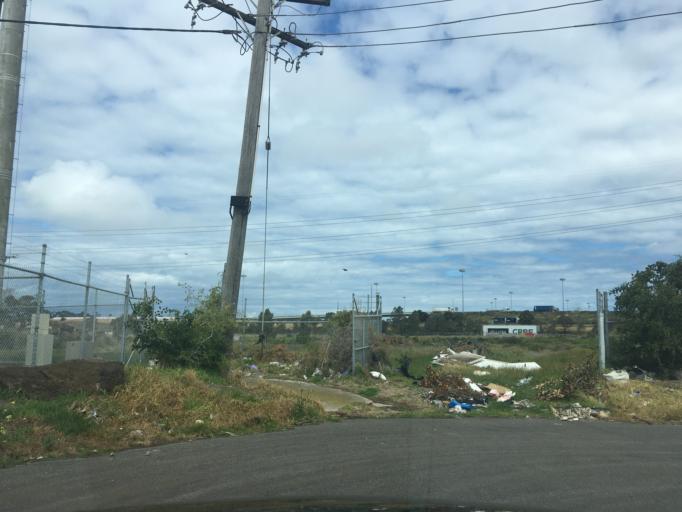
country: AU
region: Victoria
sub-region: Brimbank
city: Brooklyn
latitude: -37.8230
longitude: 144.8156
